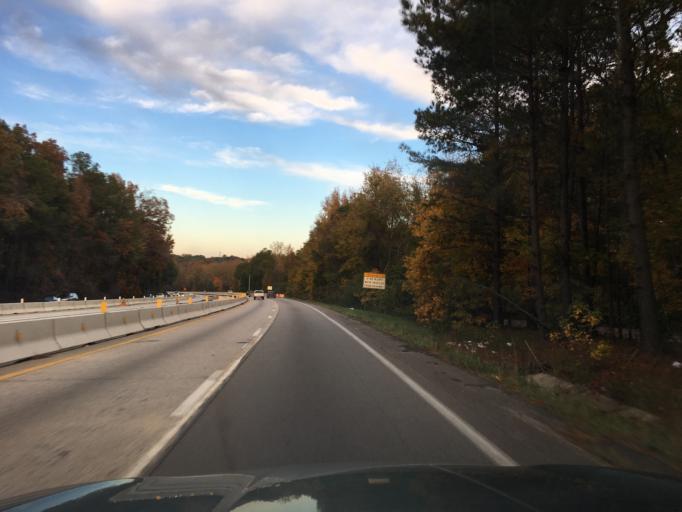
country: US
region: South Carolina
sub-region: Lexington County
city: Oak Grove
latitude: 33.9935
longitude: -81.1800
